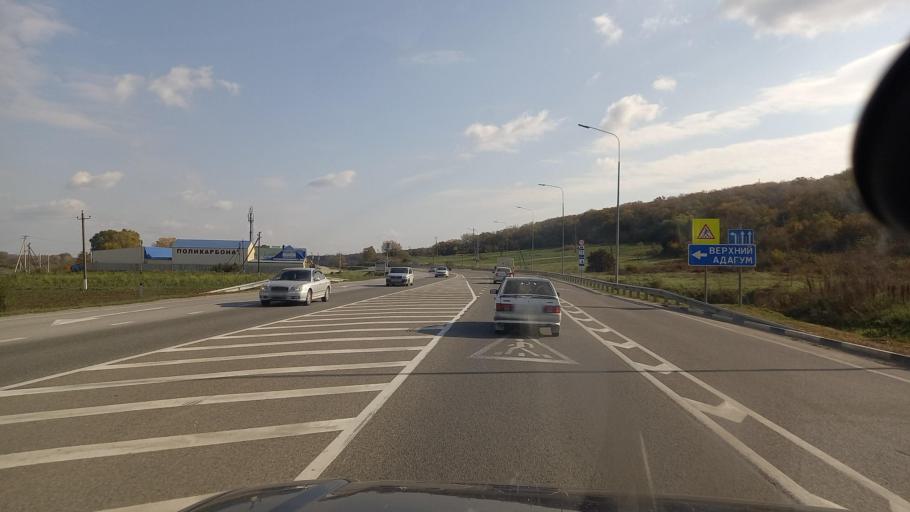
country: RU
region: Krasnodarskiy
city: Krymsk
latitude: 44.8738
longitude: 37.9197
